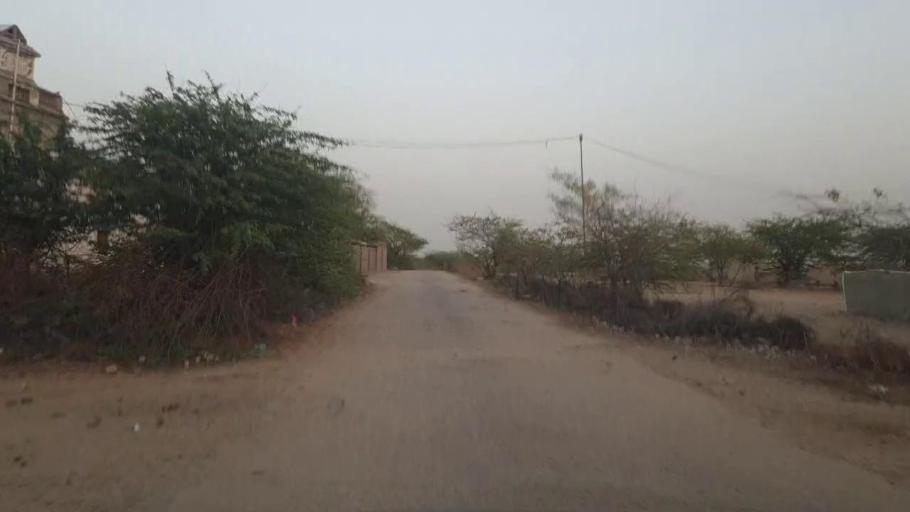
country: PK
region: Sindh
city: Chor
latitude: 25.5142
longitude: 69.8130
